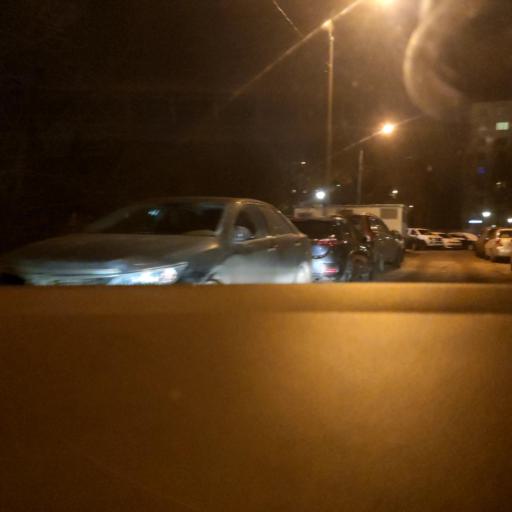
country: RU
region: Moscow
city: Solntsevo
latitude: 55.6562
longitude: 37.4083
